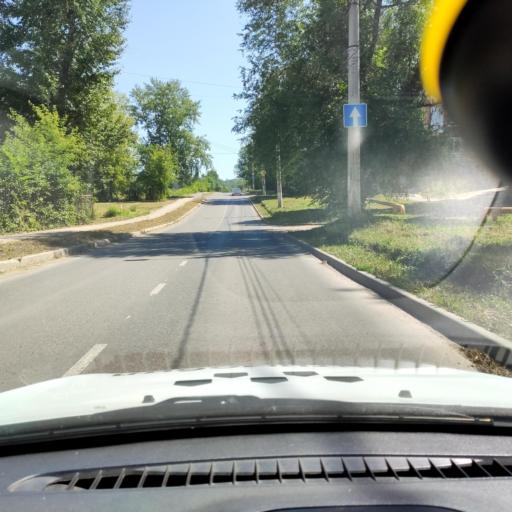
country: RU
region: Samara
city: Zhigulevsk
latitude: 53.3978
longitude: 49.5026
